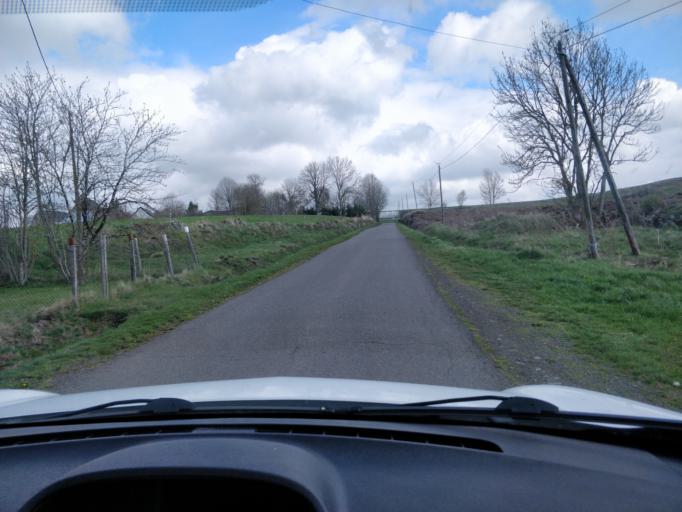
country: FR
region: Auvergne
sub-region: Departement du Cantal
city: Allanche
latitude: 45.2122
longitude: 2.9435
